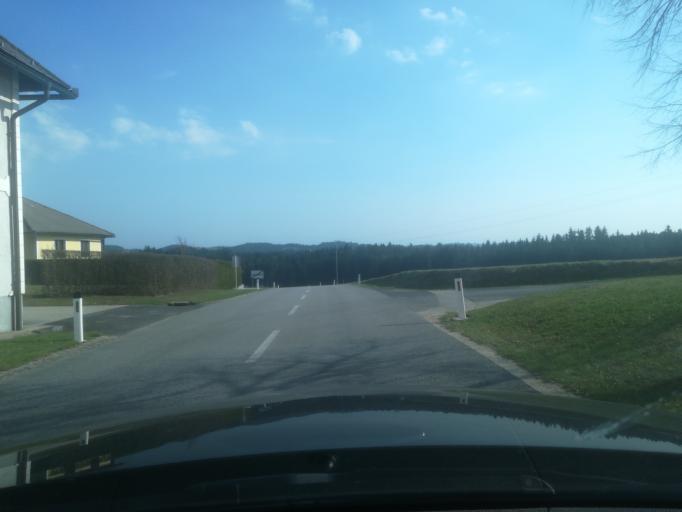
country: AT
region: Upper Austria
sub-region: Politischer Bezirk Perg
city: Perg
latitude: 48.3676
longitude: 14.6478
